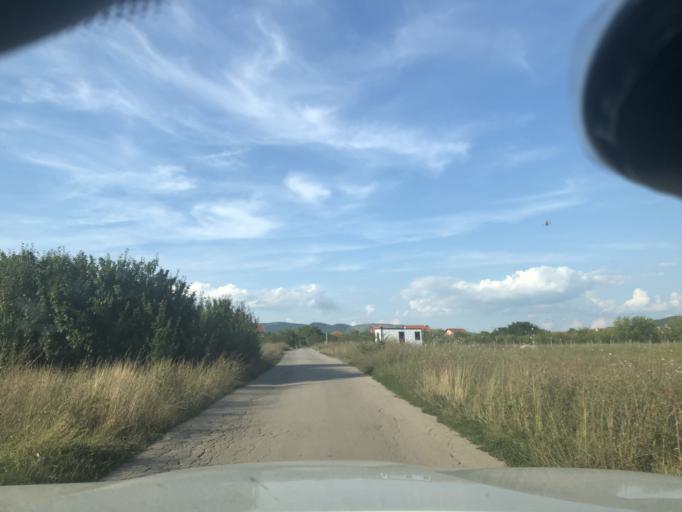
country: RS
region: Central Serbia
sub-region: Nisavski Okrug
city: Nis
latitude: 43.3248
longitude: 21.9538
